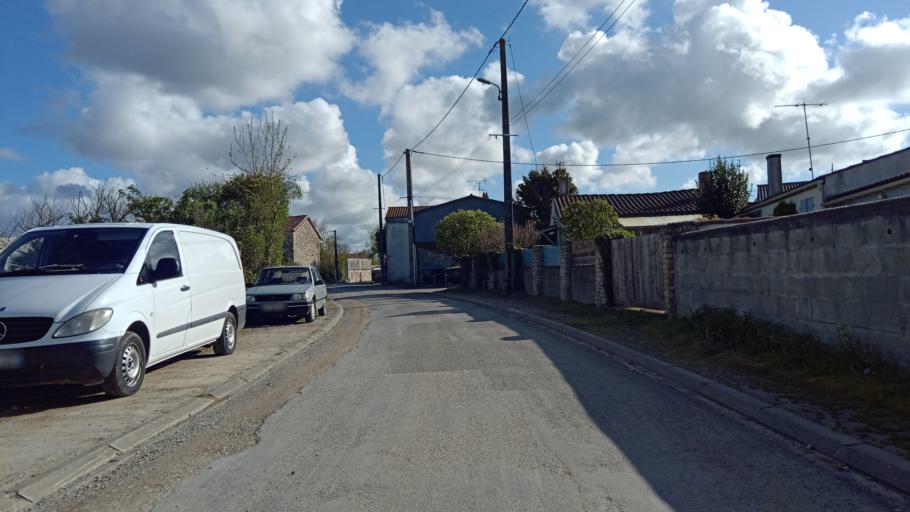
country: FR
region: Poitou-Charentes
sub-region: Departement de la Charente-Maritime
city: Verines
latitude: 46.1666
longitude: -0.9477
